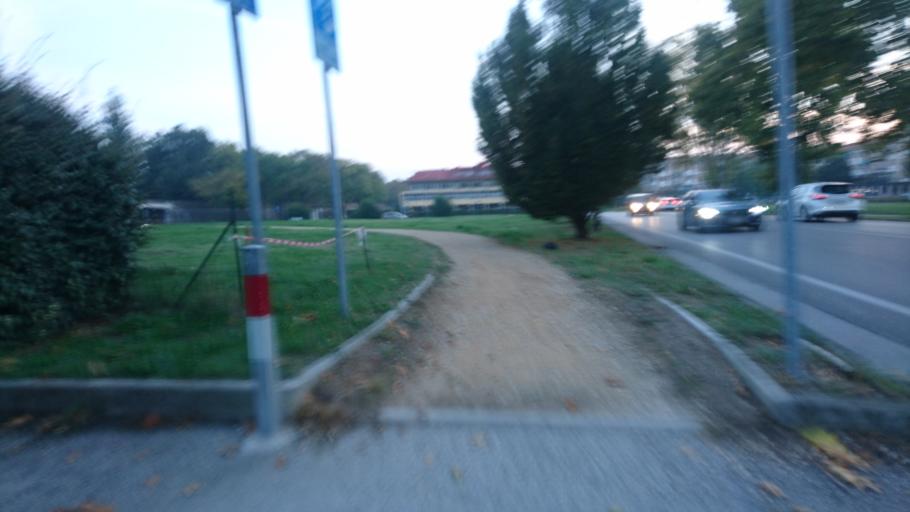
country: IT
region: Emilia-Romagna
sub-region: Provincia di Ferrara
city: Ferrara
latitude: 44.8495
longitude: 11.6142
